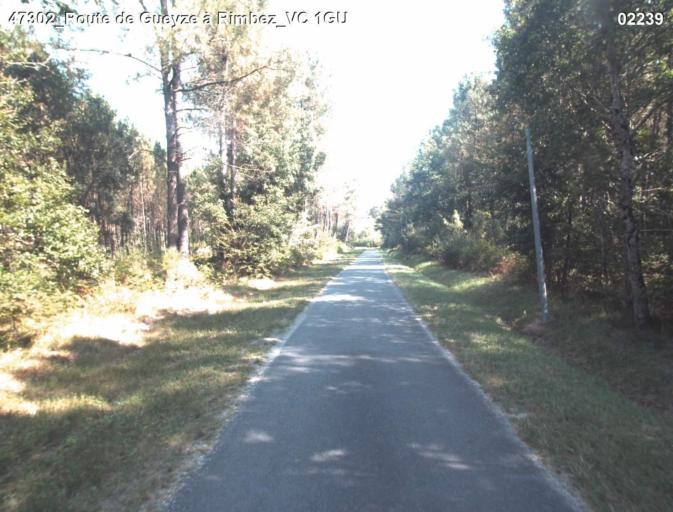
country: FR
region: Aquitaine
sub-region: Departement des Landes
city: Gabarret
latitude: 44.0425
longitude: 0.1095
